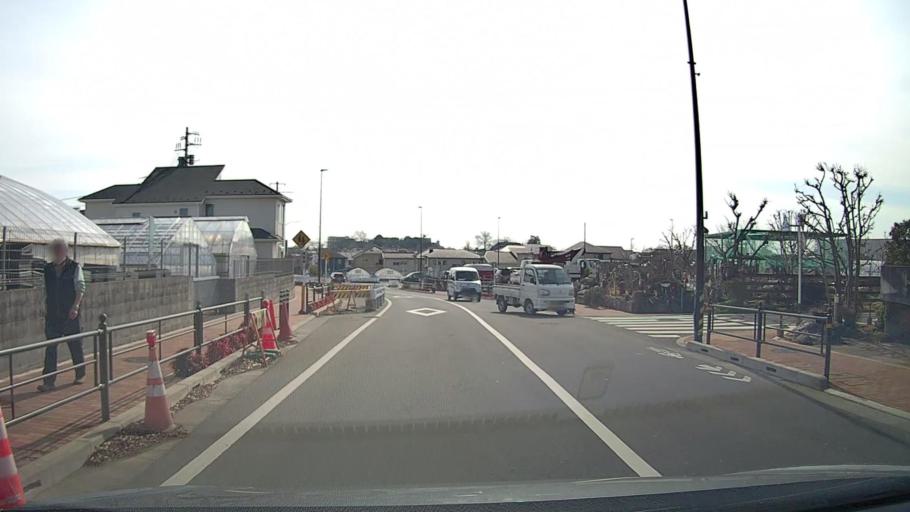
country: JP
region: Tokyo
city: Tanashicho
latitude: 35.7571
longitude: 139.5667
